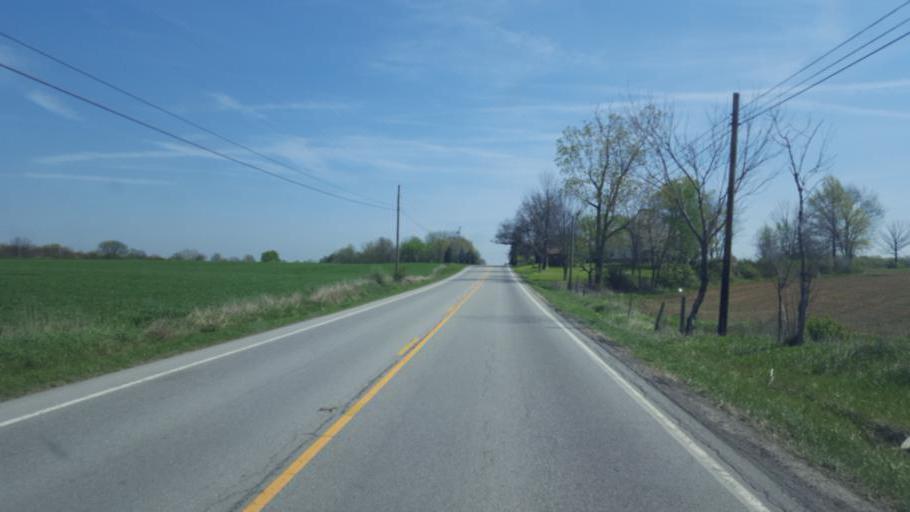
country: US
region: Ohio
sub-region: Wayne County
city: West Salem
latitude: 40.9992
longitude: -82.0706
